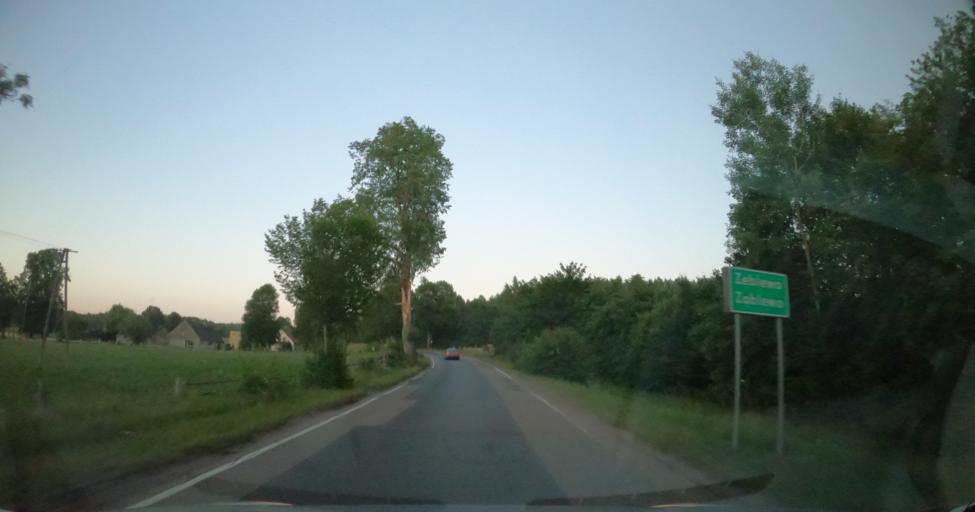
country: PL
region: Pomeranian Voivodeship
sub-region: Powiat wejherowski
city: Luzino
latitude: 54.4663
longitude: 18.0993
